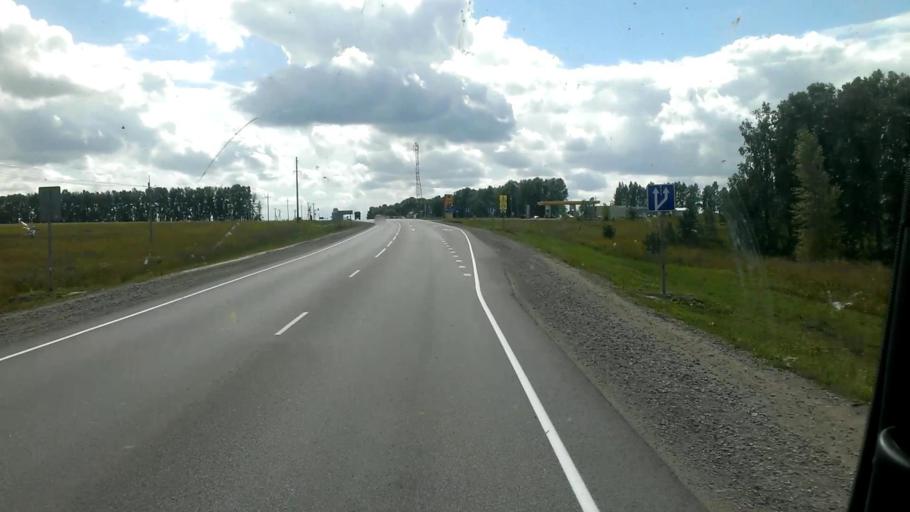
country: RU
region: Altai Krai
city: Troitskoye
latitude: 52.9704
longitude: 84.7487
